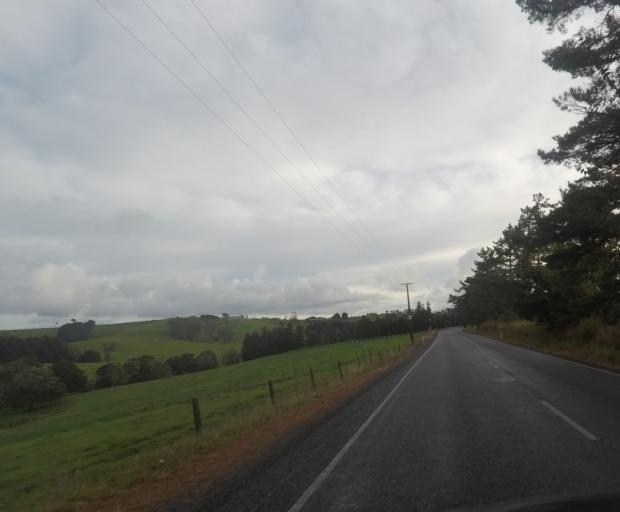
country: NZ
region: Auckland
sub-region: Auckland
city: Wellsford
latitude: -36.1876
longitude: 174.5804
